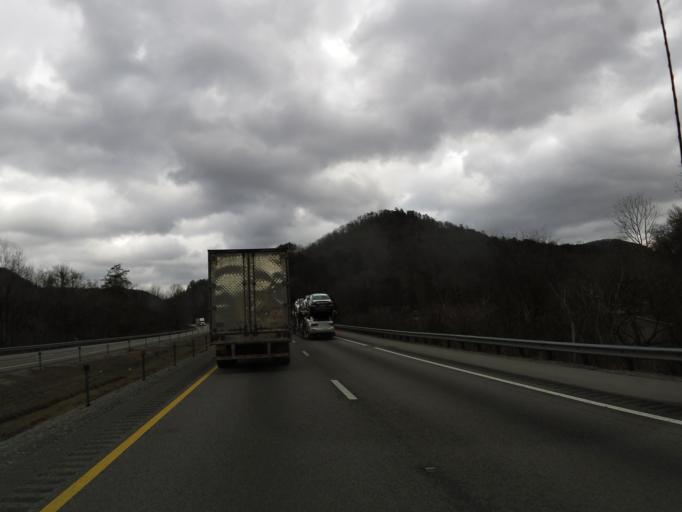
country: US
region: Georgia
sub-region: Dade County
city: Trenton
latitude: 34.9889
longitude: -85.4931
